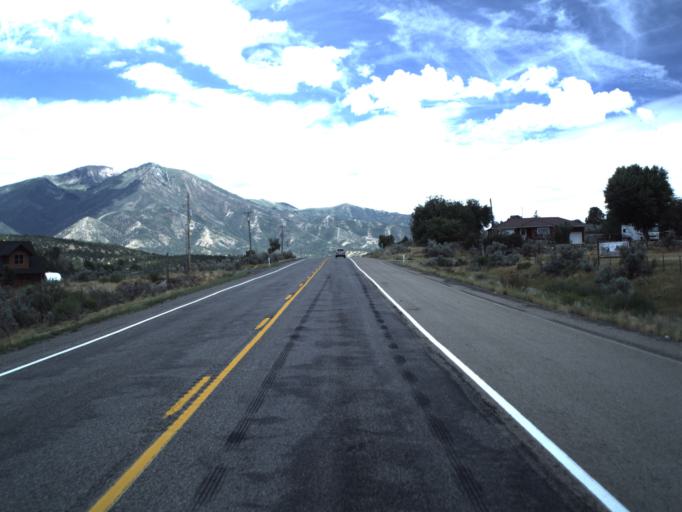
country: US
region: Utah
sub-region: Utah County
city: Woodland Hills
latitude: 39.8897
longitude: -111.5482
